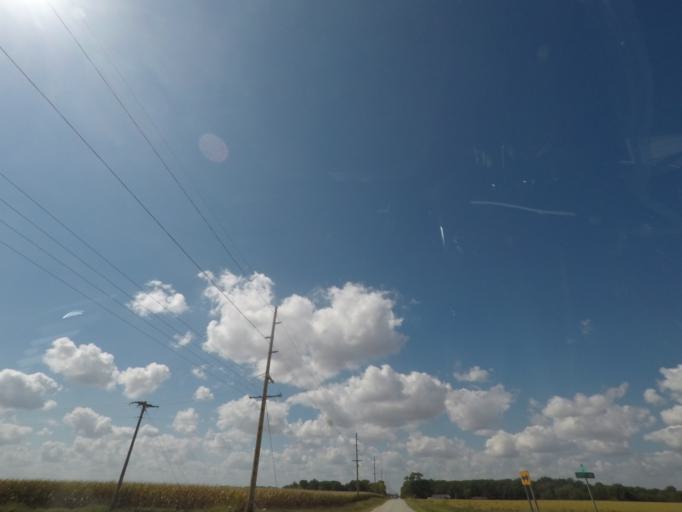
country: US
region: Iowa
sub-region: Story County
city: Nevada
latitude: 42.0343
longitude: -93.3667
